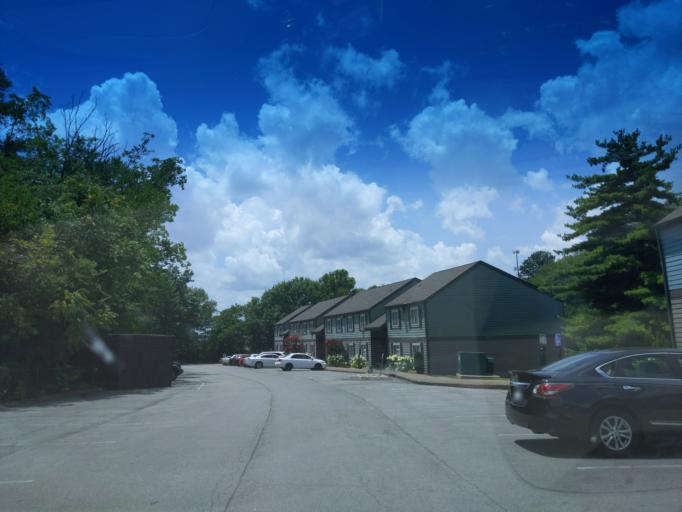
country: US
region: Tennessee
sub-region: Williamson County
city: Brentwood
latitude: 36.0364
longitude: -86.7778
